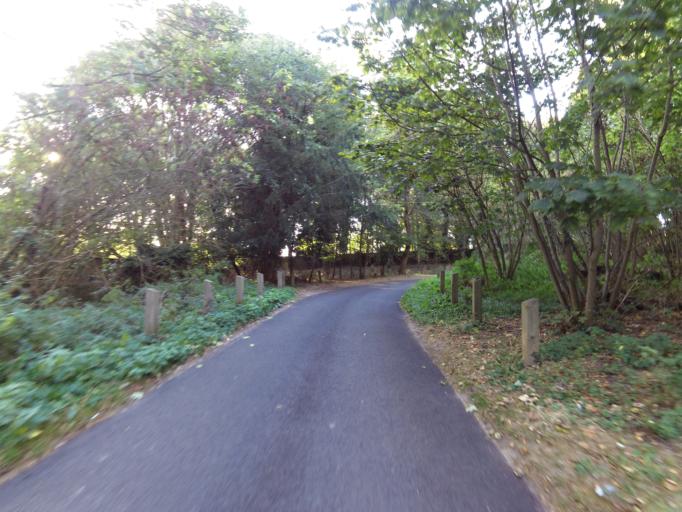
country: GB
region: England
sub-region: Suffolk
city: Kesgrave
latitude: 52.0074
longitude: 1.2323
